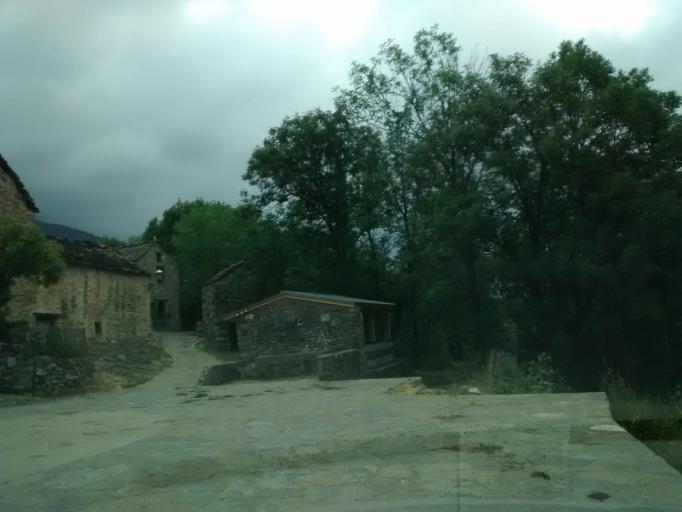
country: ES
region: Aragon
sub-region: Provincia de Huesca
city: Puertolas
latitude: 42.5958
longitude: 0.1293
